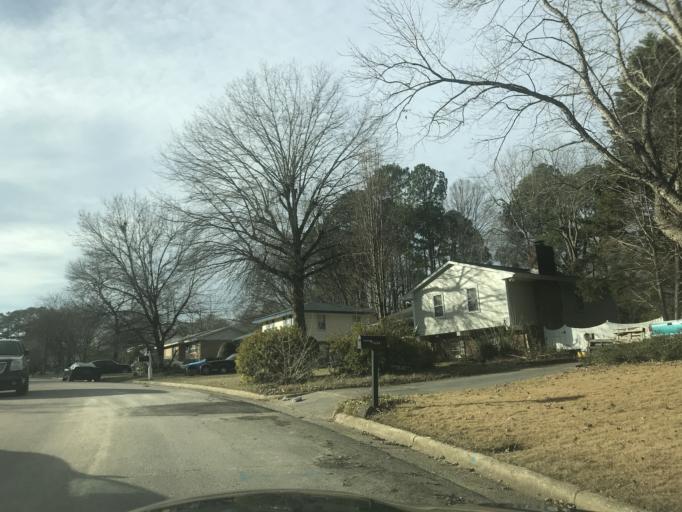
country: US
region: North Carolina
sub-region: Wake County
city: Raleigh
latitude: 35.8344
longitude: -78.5905
